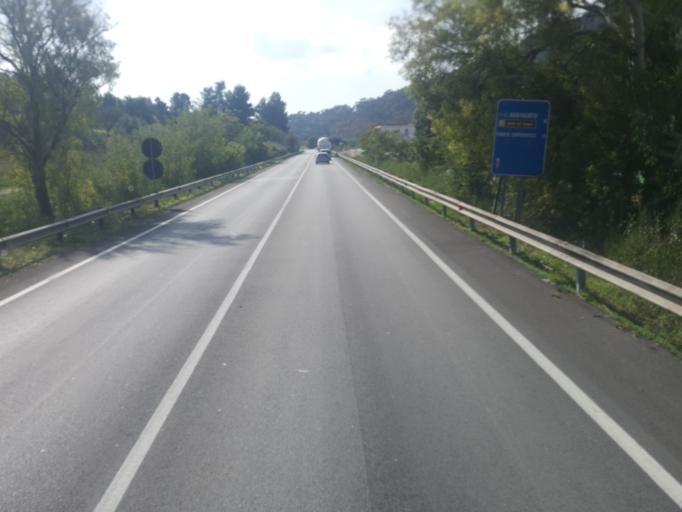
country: IT
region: Sicily
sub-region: Agrigento
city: Agrigento
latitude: 37.3086
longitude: 13.6079
